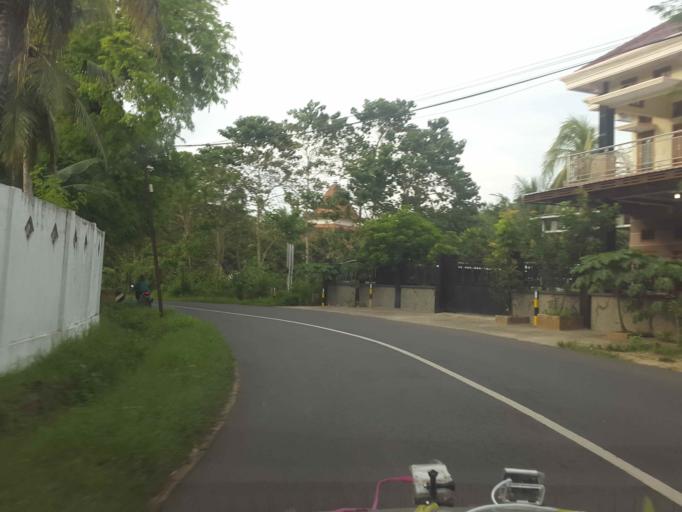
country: ID
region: East Java
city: Senmasen
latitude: -6.9870
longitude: 113.8636
